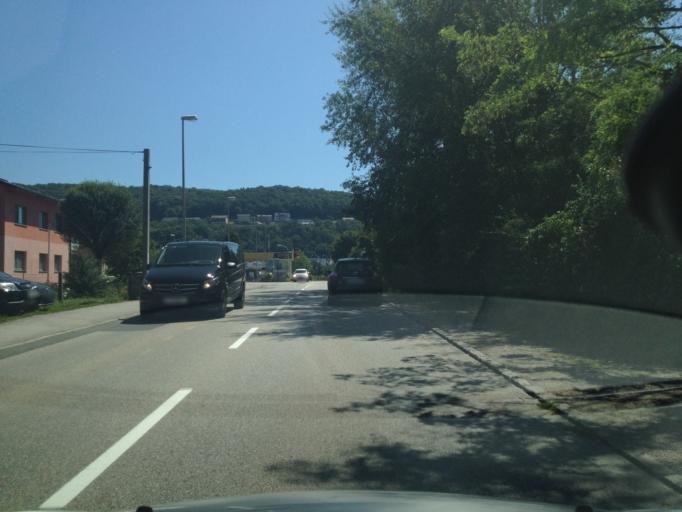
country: AT
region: Upper Austria
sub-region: Politischer Bezirk Urfahr-Umgebung
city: Steyregg
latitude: 48.2842
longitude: 14.3673
